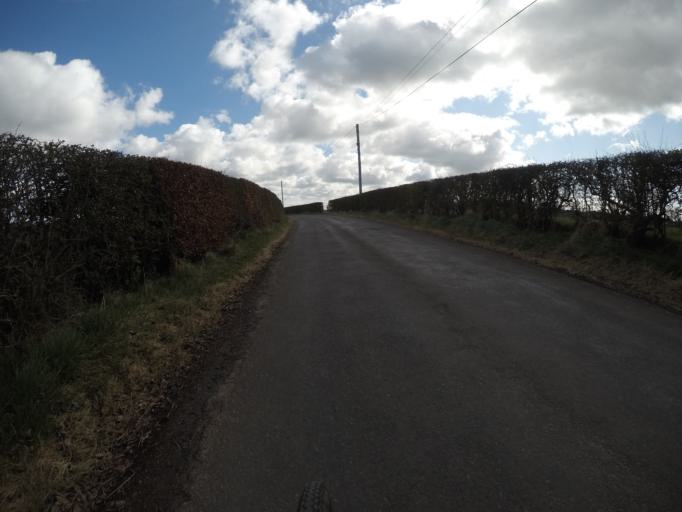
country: GB
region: Scotland
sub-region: South Ayrshire
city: Dundonald
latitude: 55.5890
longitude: -4.5883
